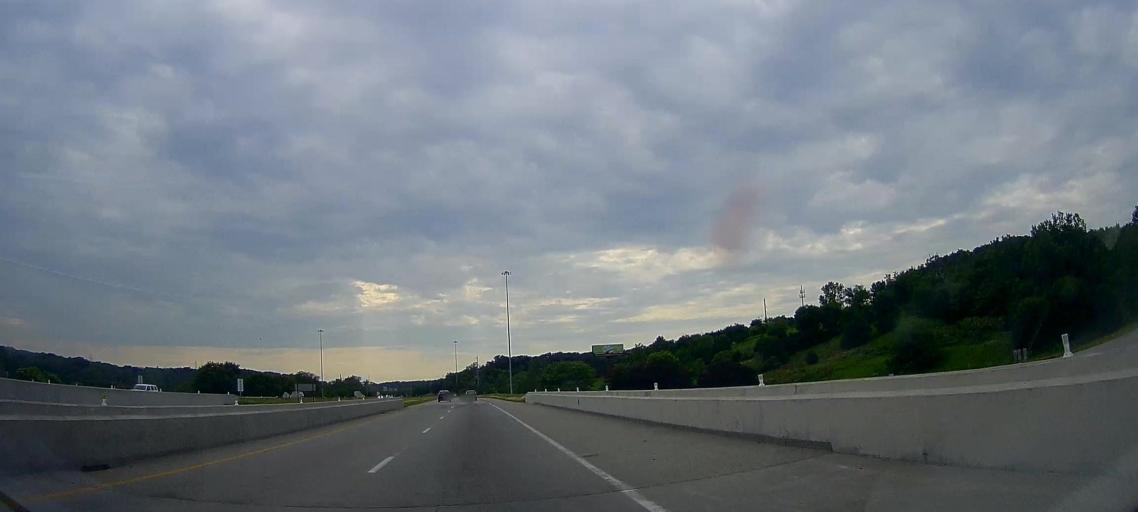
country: US
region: Iowa
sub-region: Pottawattamie County
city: Carter Lake
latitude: 41.3472
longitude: -95.9822
